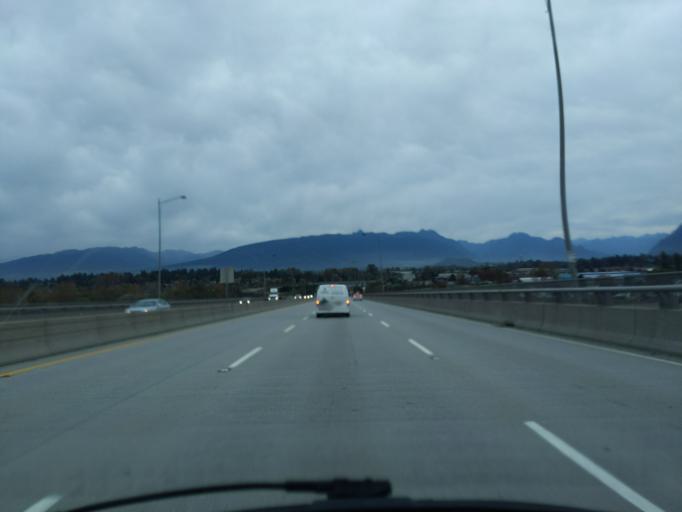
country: CA
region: British Columbia
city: Pitt Meadows
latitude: 49.2013
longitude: -122.6669
